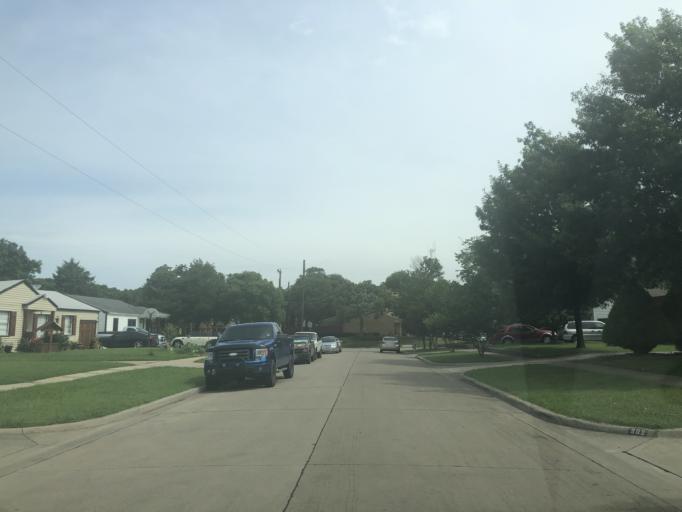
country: US
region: Texas
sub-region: Dallas County
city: Irving
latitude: 32.8116
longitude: -96.9558
